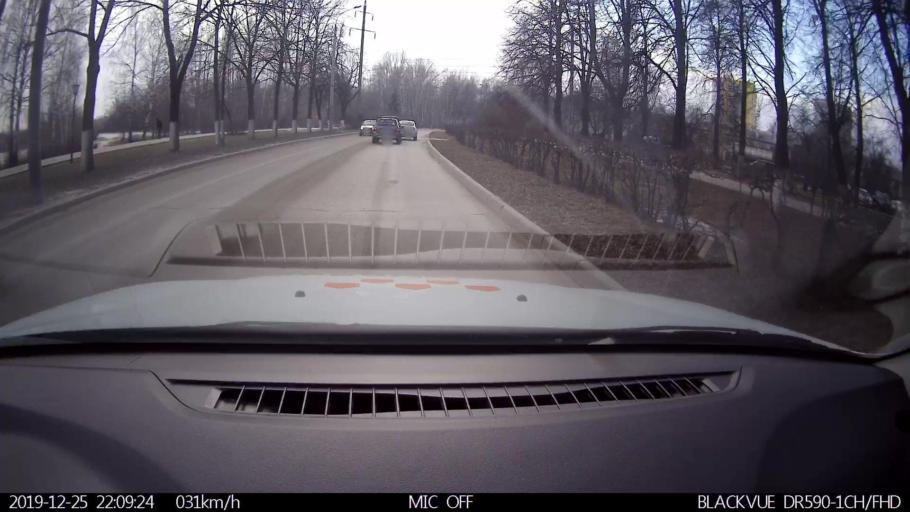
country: RU
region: Nizjnij Novgorod
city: Gorbatovka
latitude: 56.3400
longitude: 43.8479
